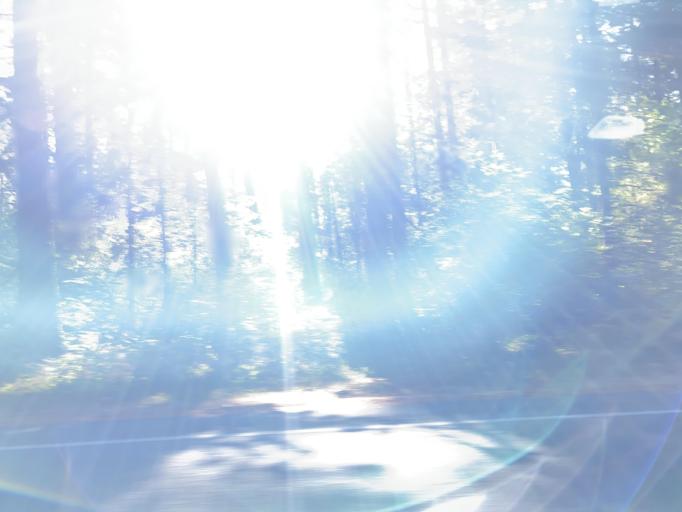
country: US
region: Washington
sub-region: Thurston County
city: Rainier
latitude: 46.9431
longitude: -122.7658
